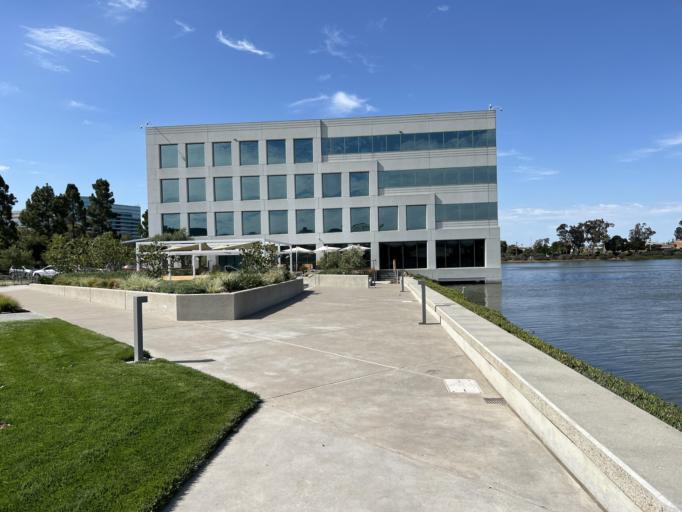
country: US
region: California
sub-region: San Mateo County
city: Redwood Shores
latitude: 37.5263
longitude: -122.2610
